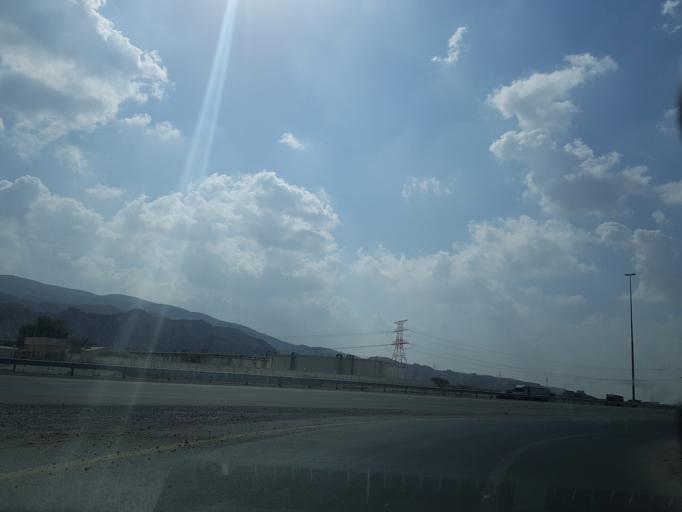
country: AE
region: Ra's al Khaymah
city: Ras al-Khaimah
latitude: 25.7733
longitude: 56.0275
